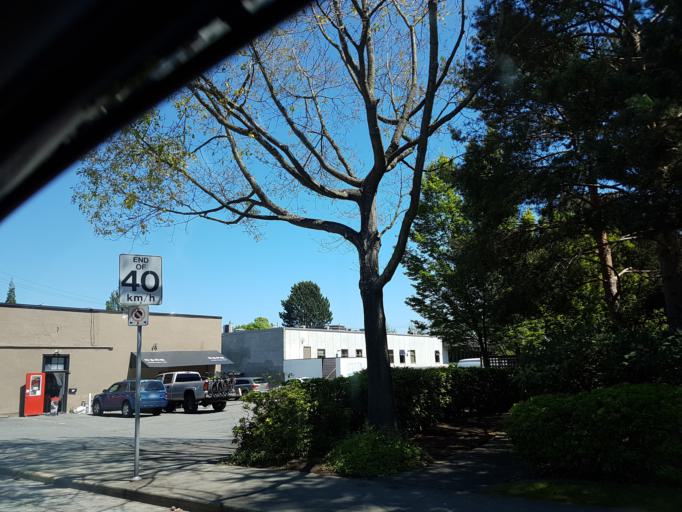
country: CA
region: British Columbia
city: Oak Bay
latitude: 48.4290
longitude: -123.3300
